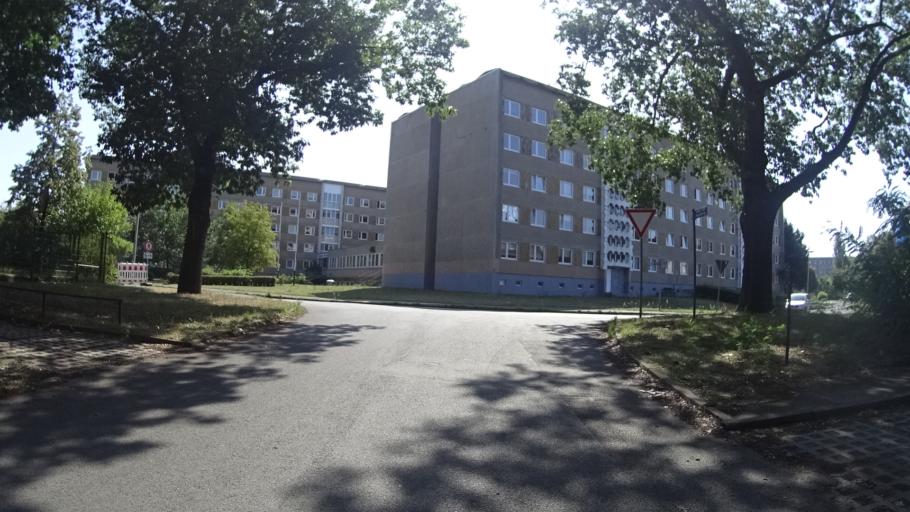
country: DE
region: Brandenburg
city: Cottbus
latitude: 51.7663
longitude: 14.3194
